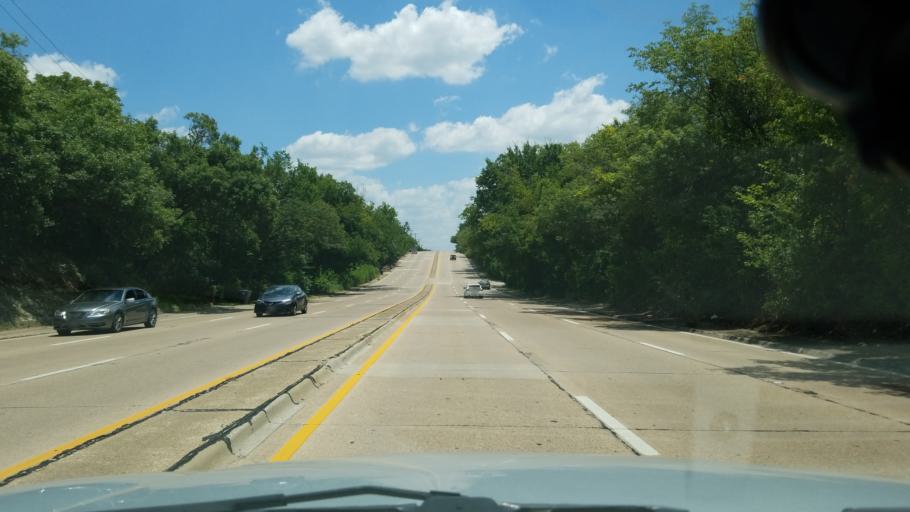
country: US
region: Texas
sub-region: Dallas County
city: Cockrell Hill
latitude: 32.6913
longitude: -96.8684
